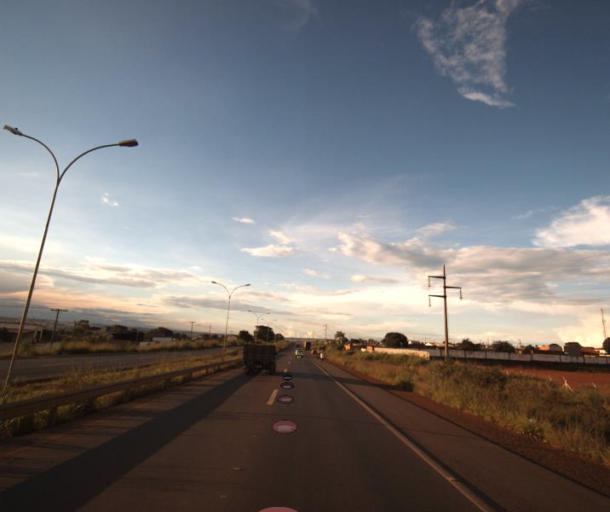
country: BR
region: Goias
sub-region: Anapolis
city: Anapolis
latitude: -16.3364
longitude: -48.9225
